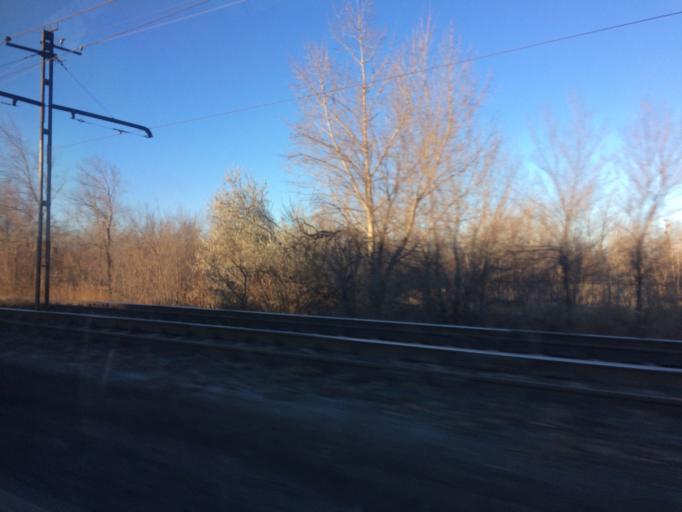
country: RU
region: Chelyabinsk
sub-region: Gorod Magnitogorsk
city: Magnitogorsk
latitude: 53.4091
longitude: 59.0313
